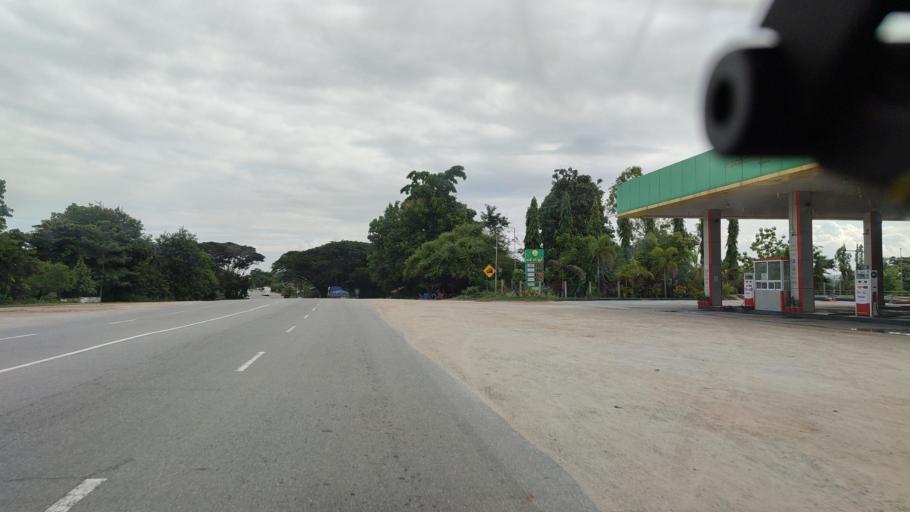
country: MM
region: Mandalay
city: Pyinmana
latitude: 19.8916
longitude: 96.2405
